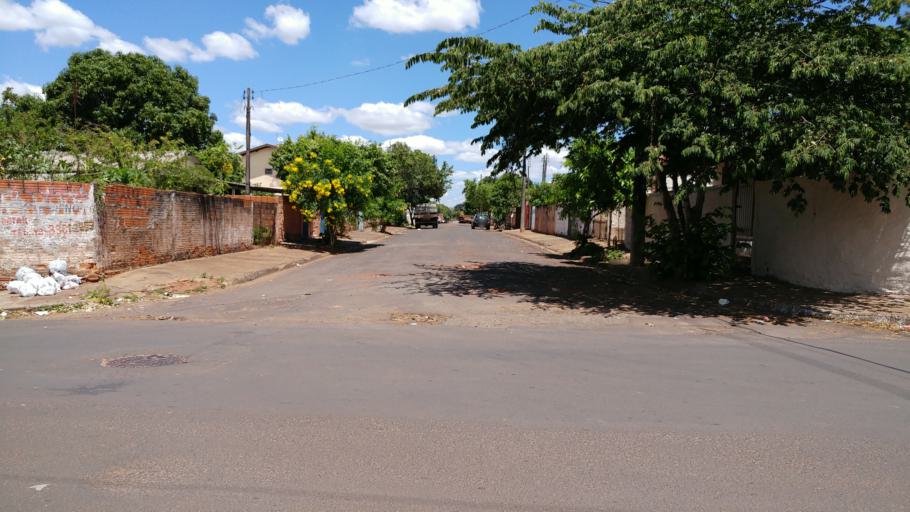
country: BR
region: Sao Paulo
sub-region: Paraguacu Paulista
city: Paraguacu Paulista
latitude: -22.4065
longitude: -50.5700
